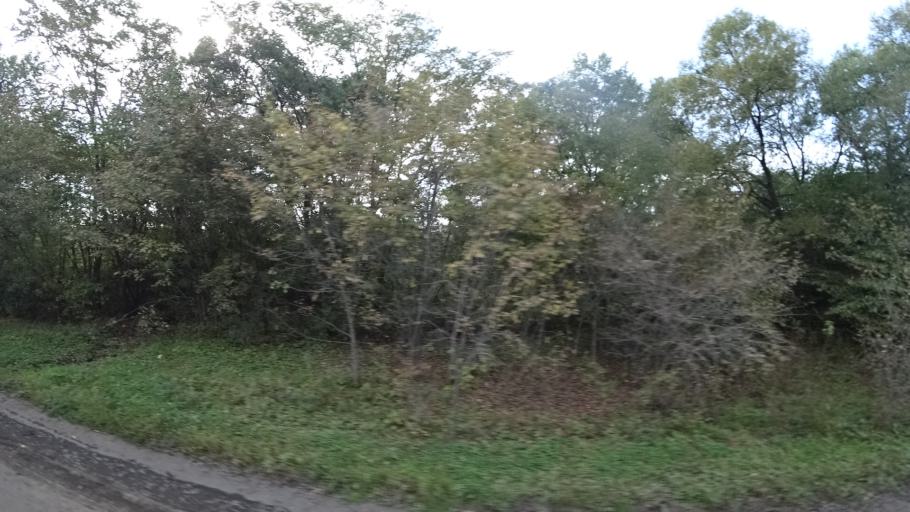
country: RU
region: Amur
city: Arkhara
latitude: 49.3553
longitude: 130.1102
